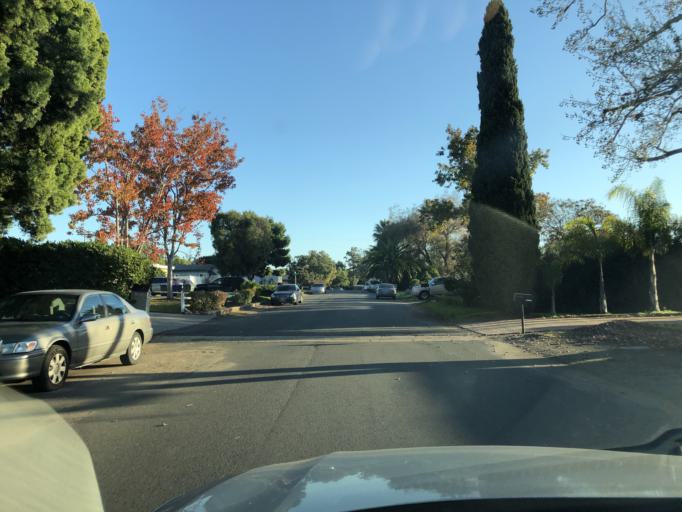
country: US
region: California
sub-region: San Diego County
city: Bonita
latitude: 32.6542
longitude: -117.0582
